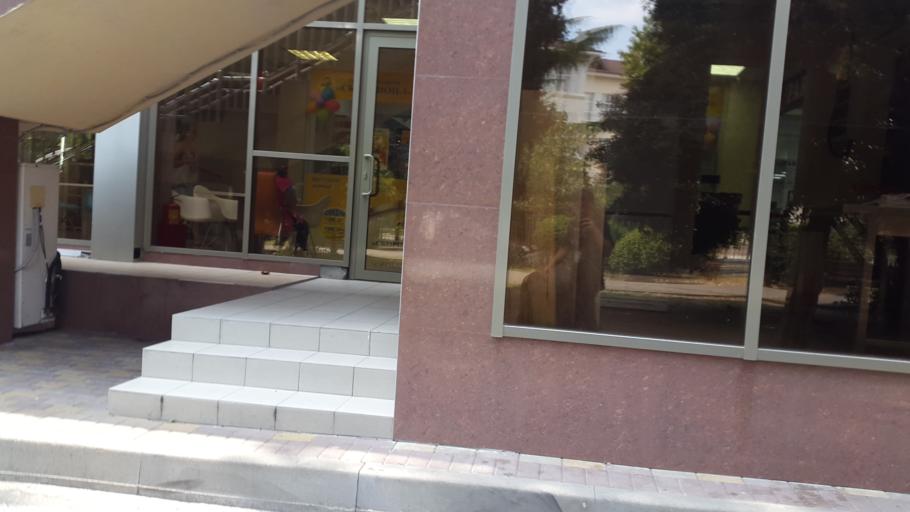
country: RU
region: Krasnodarskiy
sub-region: Sochi City
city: Sochi
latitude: 43.5970
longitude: 39.7223
